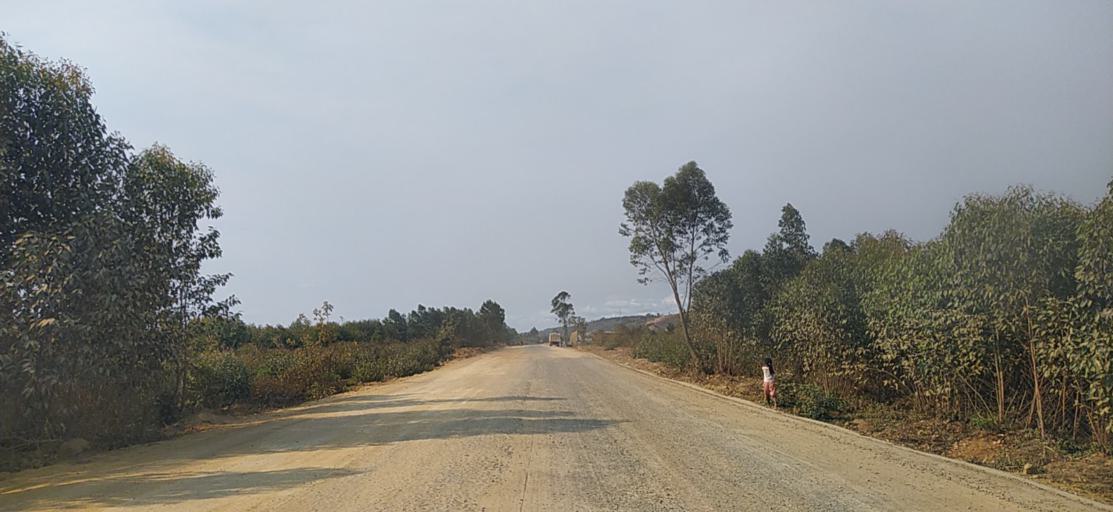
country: MG
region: Alaotra Mangoro
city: Moramanga
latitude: -18.6718
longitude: 48.2736
